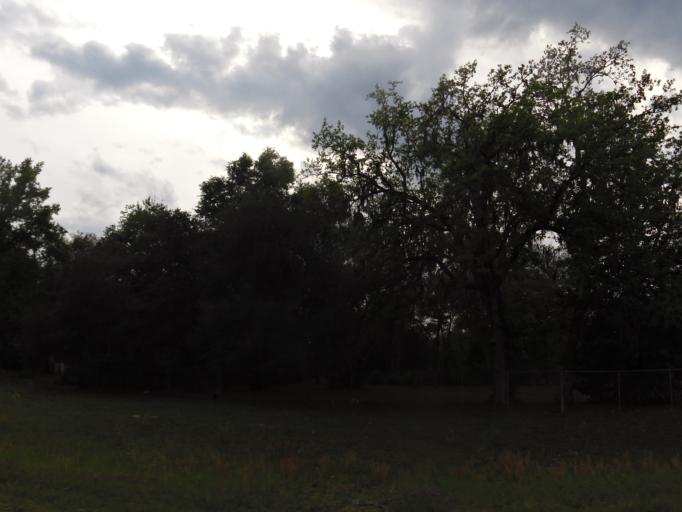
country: US
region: Georgia
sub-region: Charlton County
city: Folkston
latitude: 30.8113
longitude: -81.9981
